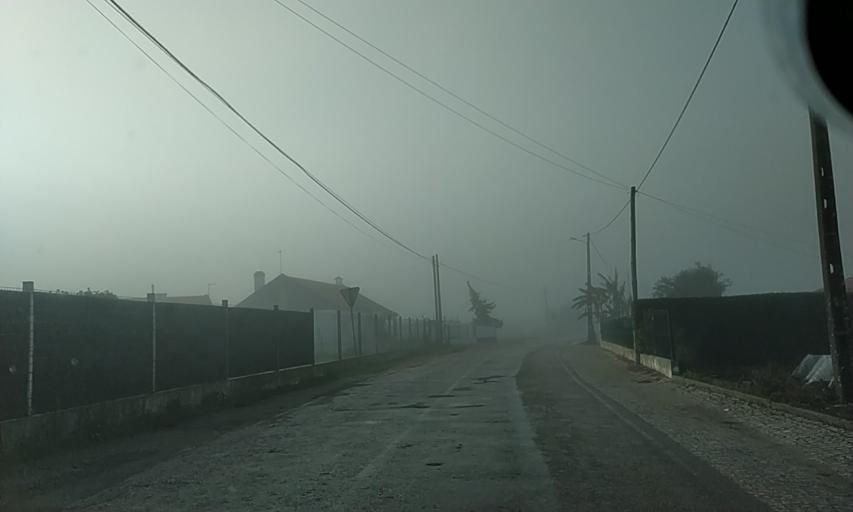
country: PT
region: Setubal
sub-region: Palmela
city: Pinhal Novo
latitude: 38.6136
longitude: -8.8834
